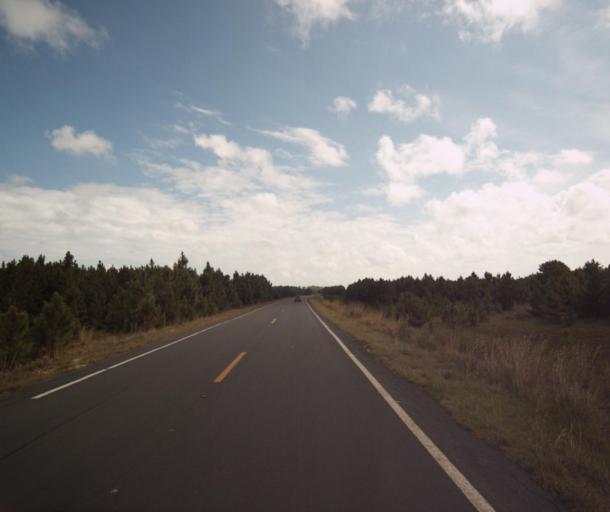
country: BR
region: Rio Grande do Sul
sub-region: Sao Lourenco Do Sul
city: Sao Lourenco do Sul
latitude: -31.4410
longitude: -51.1995
